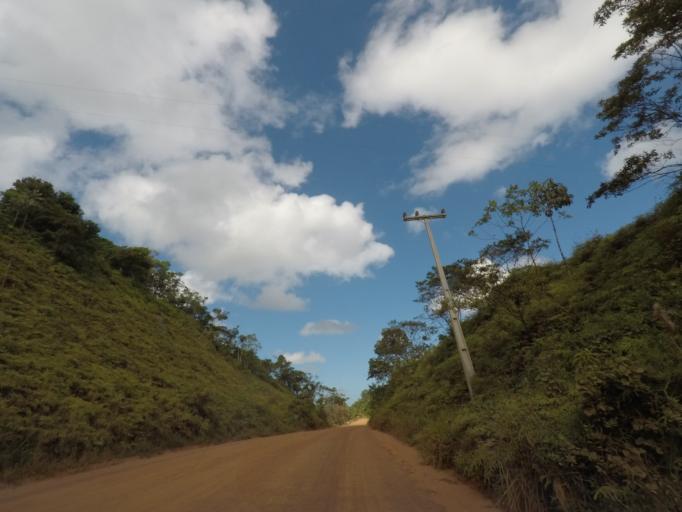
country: BR
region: Bahia
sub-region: Itacare
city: Itacare
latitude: -14.2202
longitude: -39.0745
